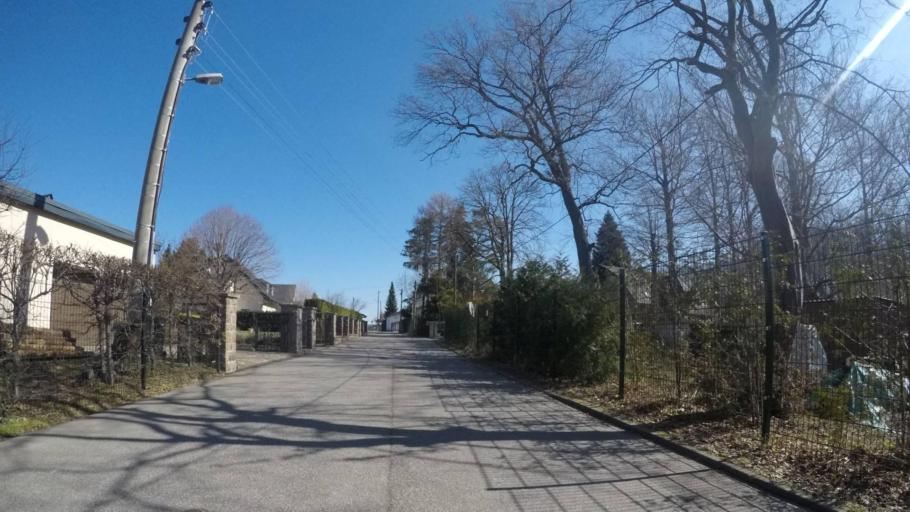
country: DE
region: Saxony
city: Limbach-Oberfrohna
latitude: 50.8683
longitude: 12.7812
